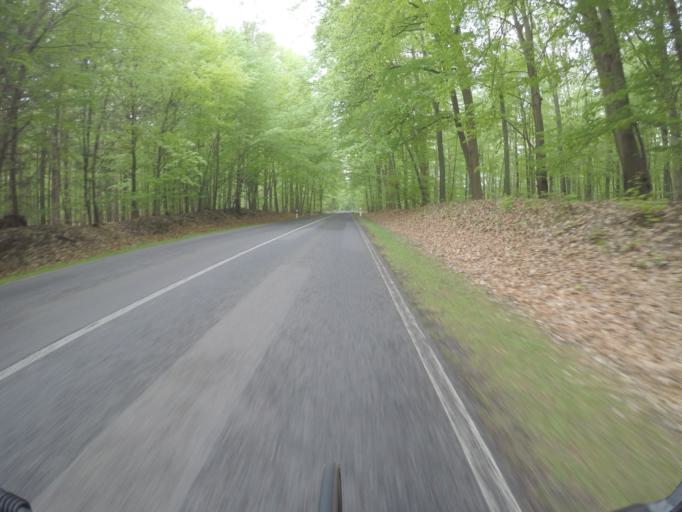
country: DE
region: Brandenburg
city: Joachimsthal
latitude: 52.9301
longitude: 13.7339
